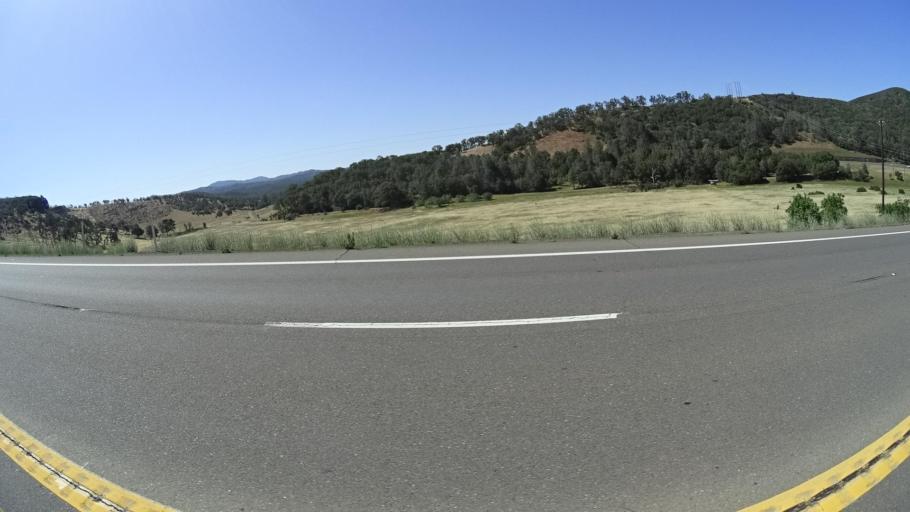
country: US
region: California
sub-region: Lake County
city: Clearlake
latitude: 39.0104
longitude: -122.6081
